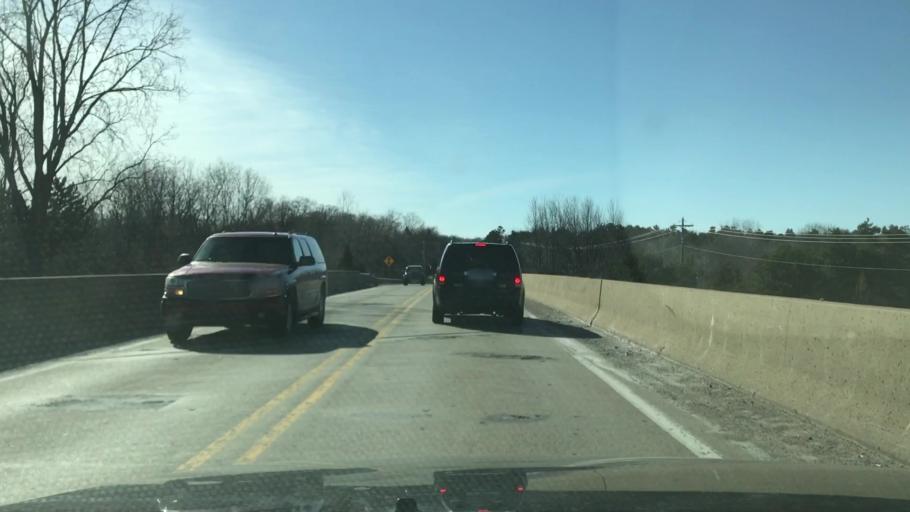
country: US
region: Michigan
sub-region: Kent County
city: East Grand Rapids
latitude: 42.9199
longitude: -85.5464
